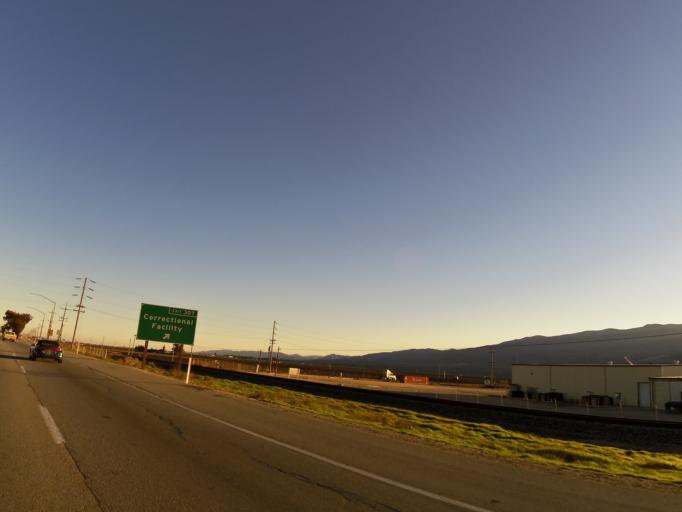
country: US
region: California
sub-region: Monterey County
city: Gonzales
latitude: 36.4675
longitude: -121.3927
